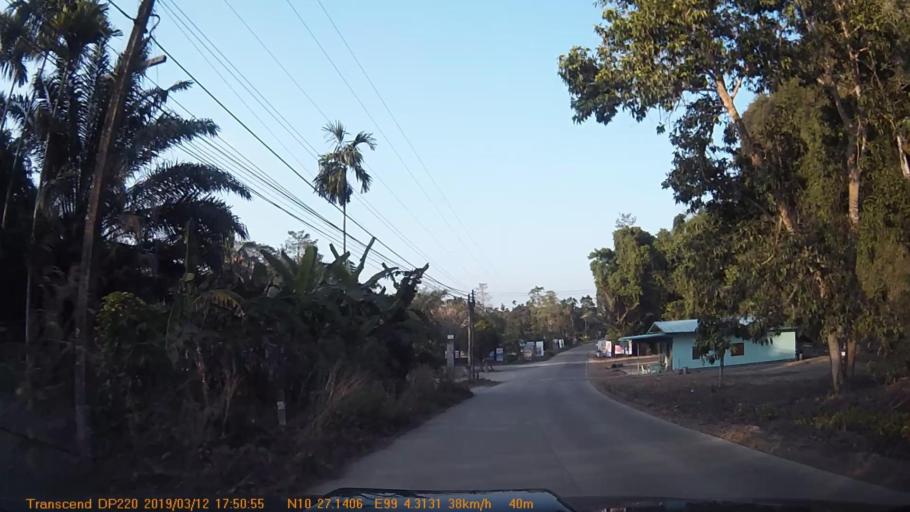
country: TH
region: Chumphon
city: Chumphon
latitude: 10.4531
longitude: 99.0720
